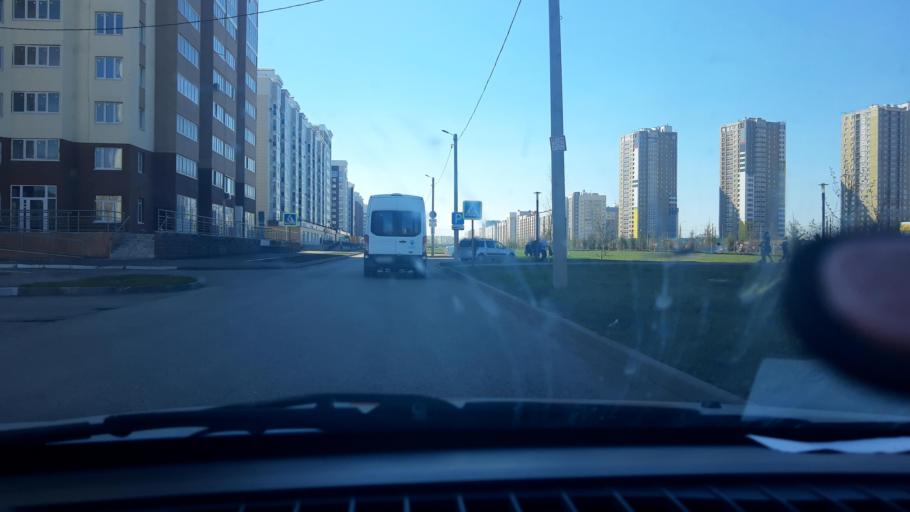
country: RU
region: Bashkortostan
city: Sterlitamak
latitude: 53.6292
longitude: 55.9009
